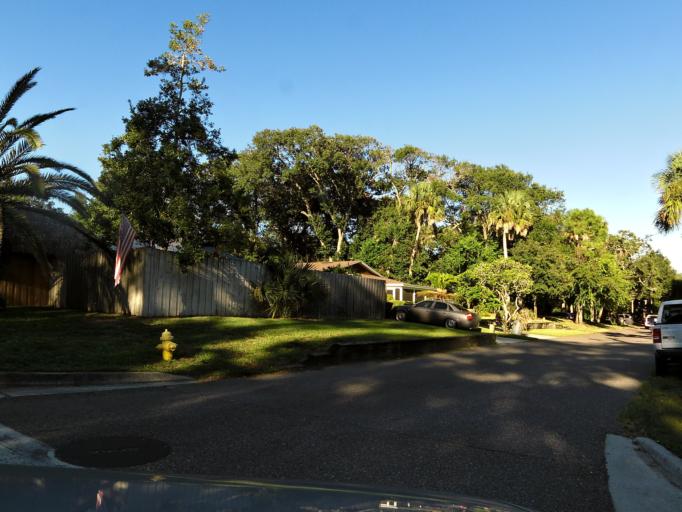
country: US
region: Florida
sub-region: Duval County
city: Atlantic Beach
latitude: 30.3268
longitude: -81.4000
